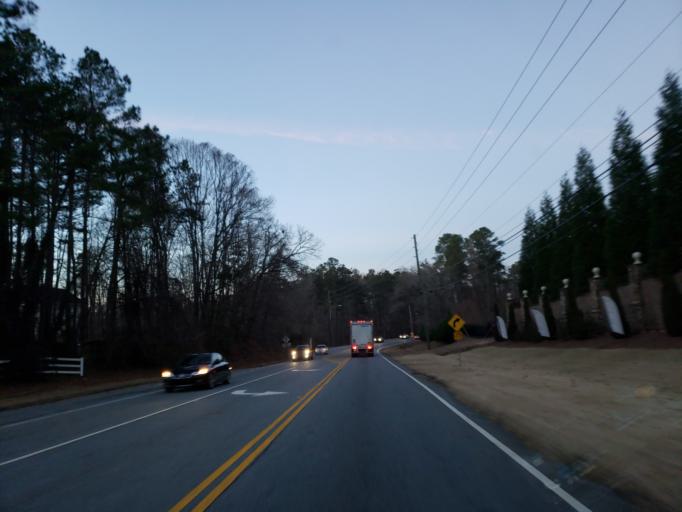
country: US
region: Georgia
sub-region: Cobb County
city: Powder Springs
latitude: 33.9466
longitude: -84.7045
